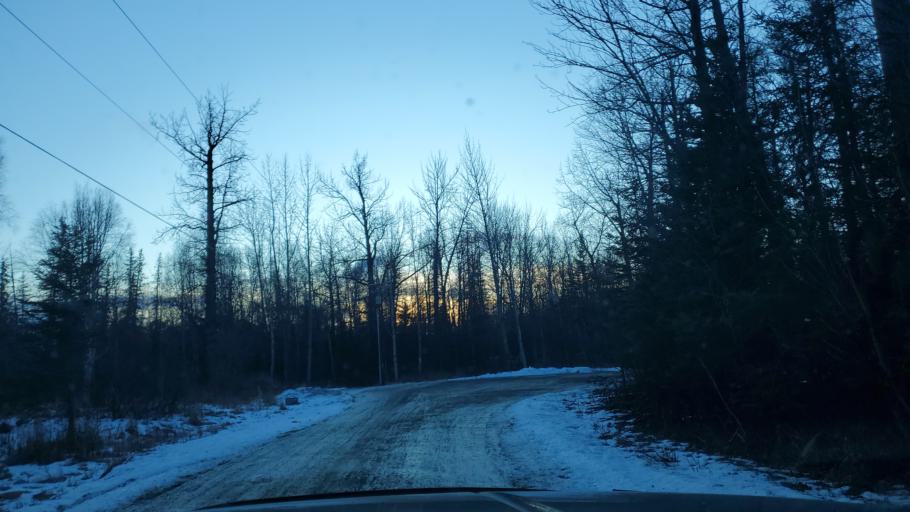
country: US
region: Alaska
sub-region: Matanuska-Susitna Borough
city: Lakes
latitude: 61.6652
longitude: -149.3410
